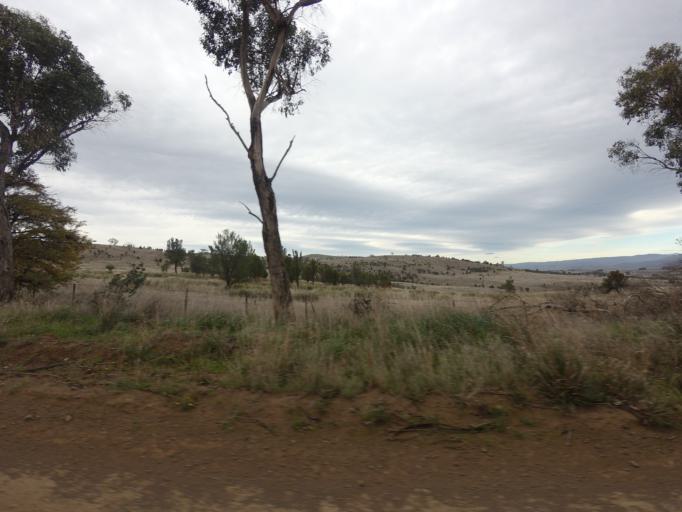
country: AU
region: Tasmania
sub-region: Derwent Valley
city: New Norfolk
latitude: -42.5540
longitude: 146.8921
